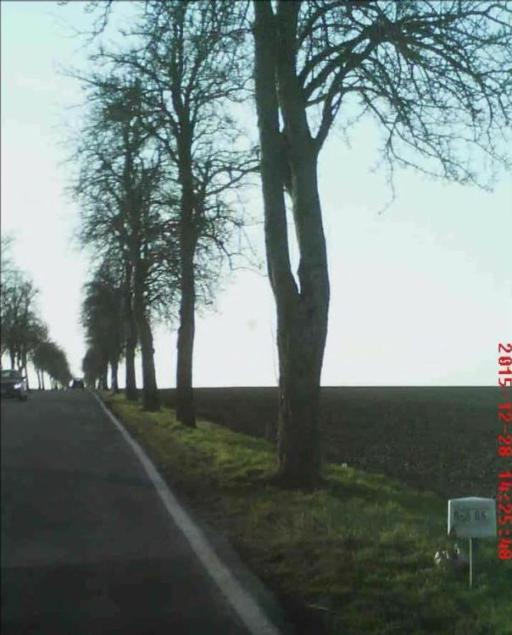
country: DE
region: Thuringia
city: Pfiffelbach
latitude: 51.0583
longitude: 11.4351
